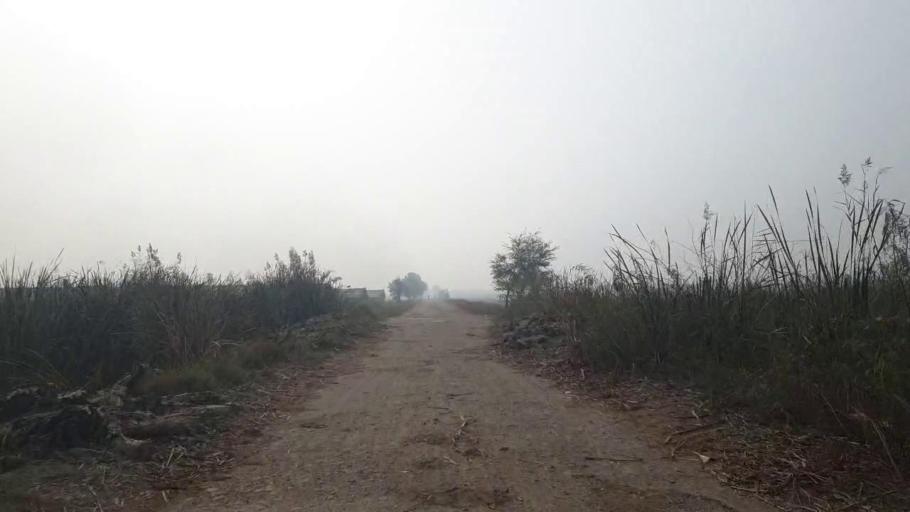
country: PK
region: Sindh
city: Tando Adam
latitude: 25.7771
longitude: 68.6072
